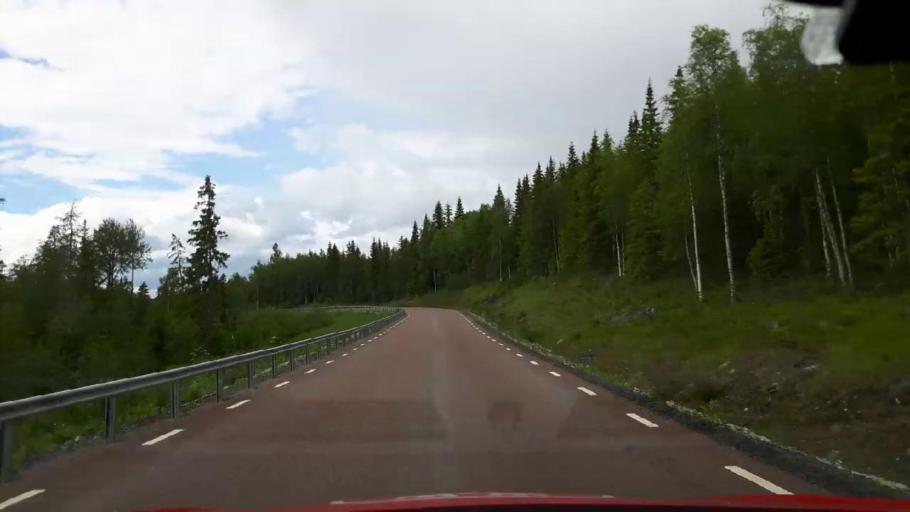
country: SE
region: Jaemtland
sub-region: Krokoms Kommun
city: Valla
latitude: 64.0890
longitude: 14.0582
